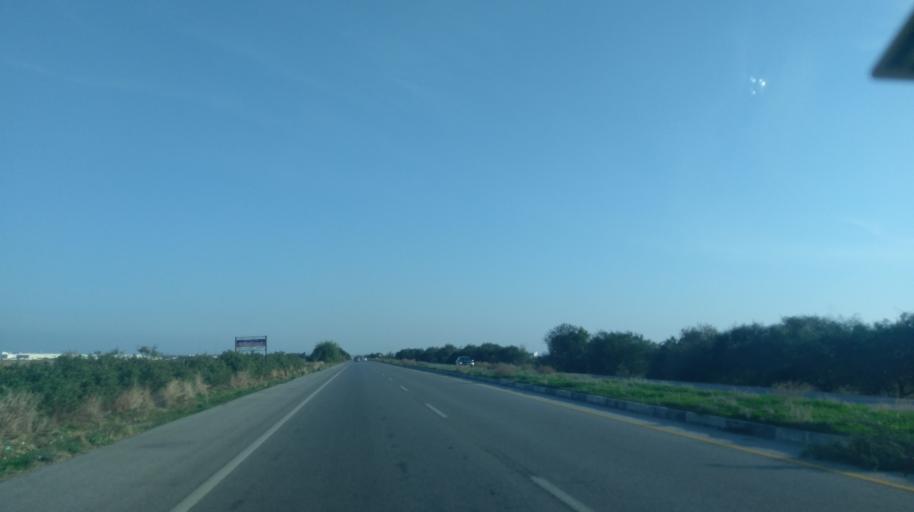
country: CY
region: Ammochostos
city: Acheritou
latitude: 35.1447
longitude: 33.8590
